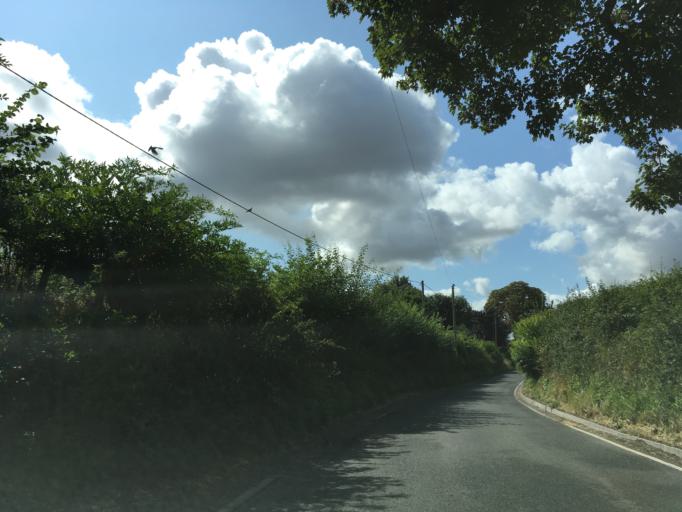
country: GB
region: England
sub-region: Hampshire
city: Kings Worthy
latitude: 51.1702
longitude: -1.3778
